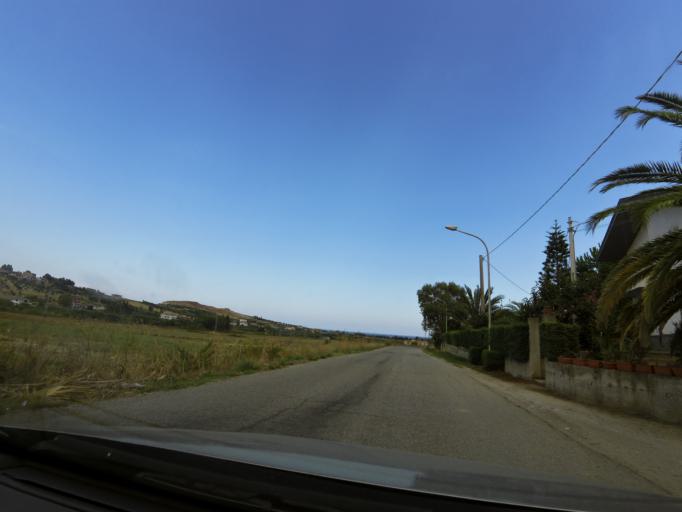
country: IT
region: Calabria
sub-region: Provincia di Reggio Calabria
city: Monasterace
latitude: 38.4253
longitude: 16.5361
